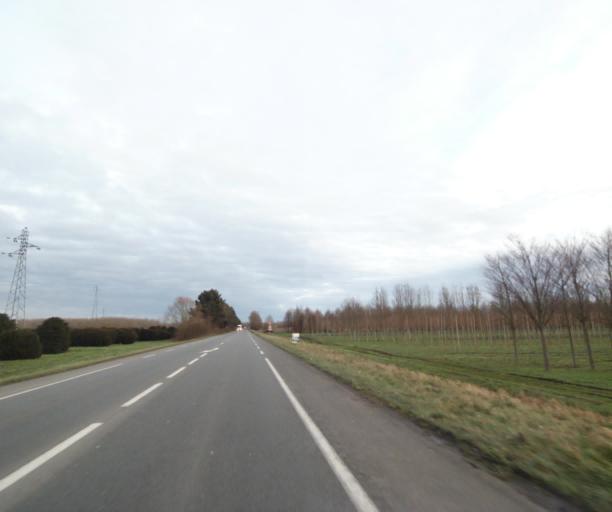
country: FR
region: Nord-Pas-de-Calais
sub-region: Departement du Nord
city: Vicq
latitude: 50.4216
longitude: 3.5950
